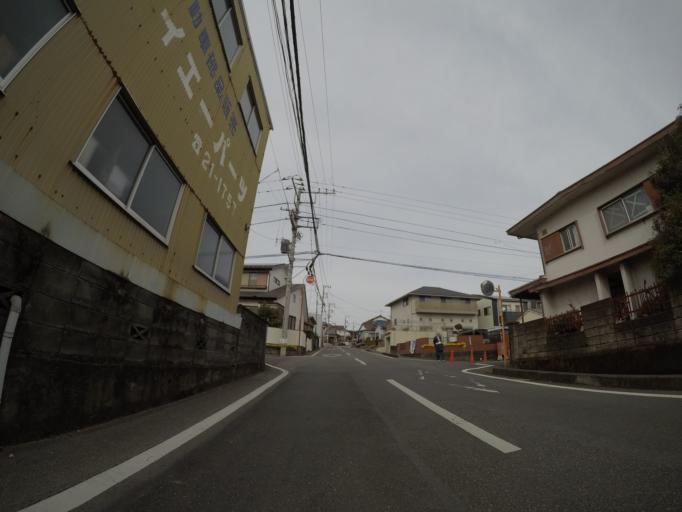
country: JP
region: Shizuoka
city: Fuji
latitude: 35.1843
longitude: 138.6889
